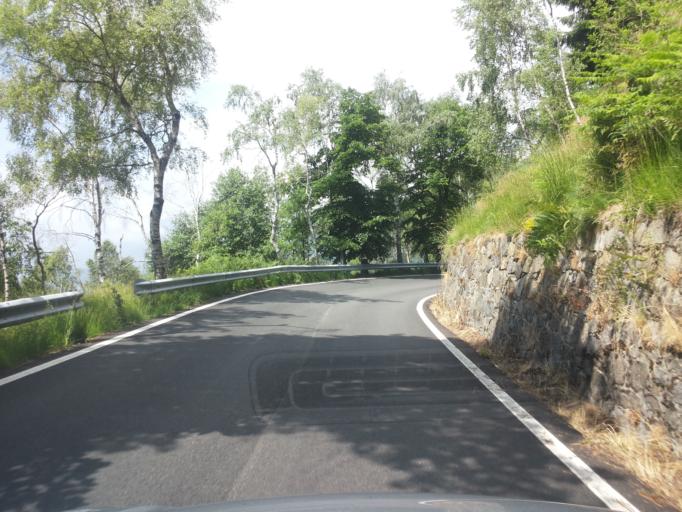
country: IT
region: Piedmont
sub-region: Provincia di Biella
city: Mosso Santa Maria
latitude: 45.6622
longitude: 8.1231
